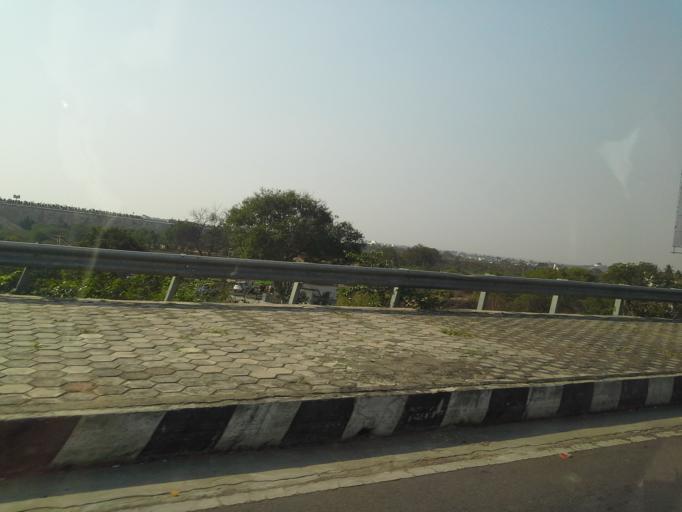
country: IN
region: Telangana
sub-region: Rangareddi
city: Sriramnagar
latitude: 17.2489
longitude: 78.3827
